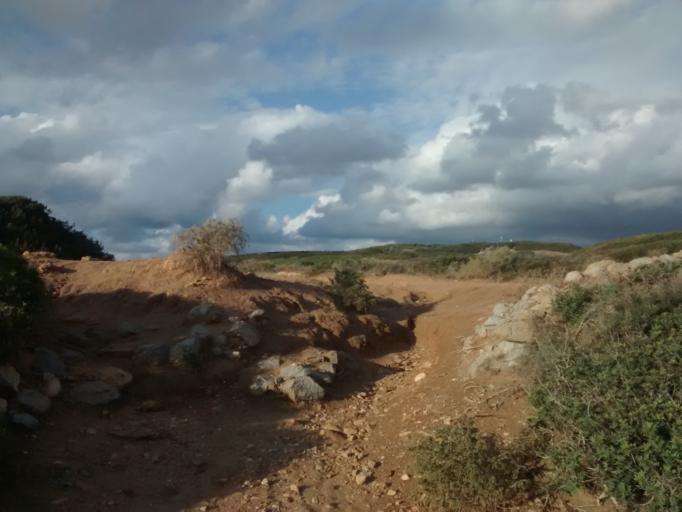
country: IT
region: Sardinia
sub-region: Provincia di Oristano
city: Narbolia
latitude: 40.0943
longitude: 8.4896
